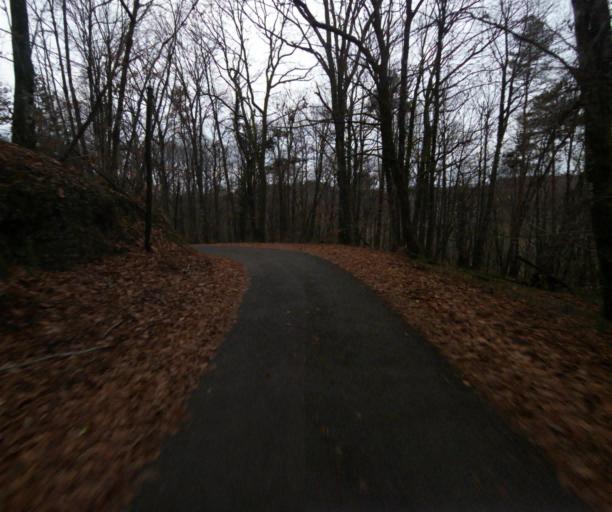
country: FR
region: Limousin
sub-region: Departement de la Correze
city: Saint-Mexant
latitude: 45.2444
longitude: 1.6570
